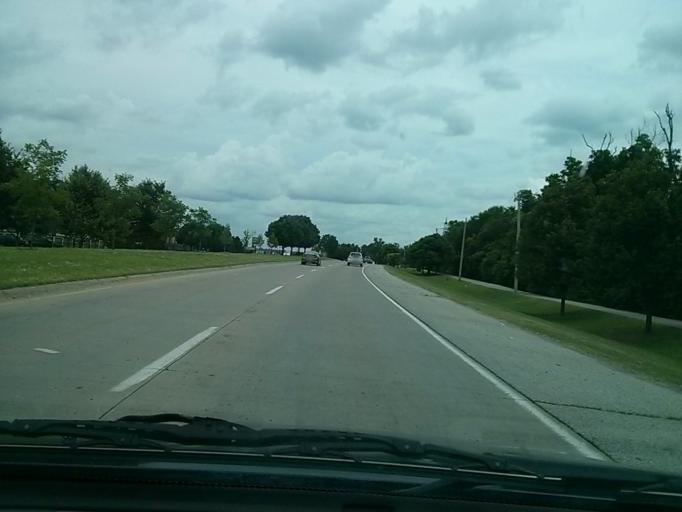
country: US
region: Oklahoma
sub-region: Tulsa County
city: Jenks
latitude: 36.0296
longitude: -95.9525
